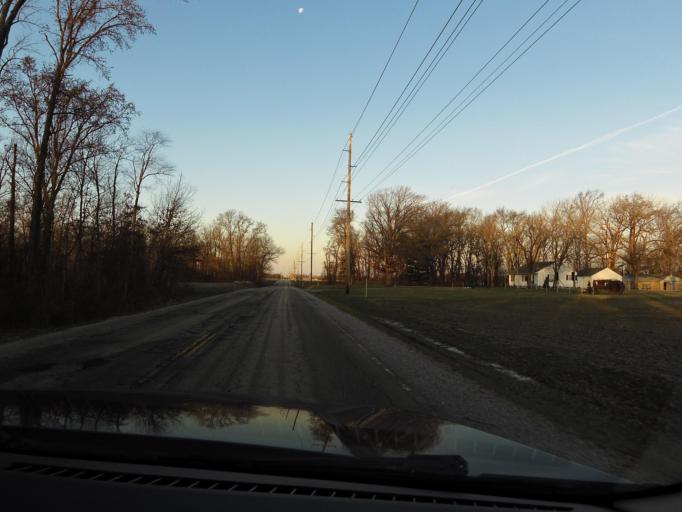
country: US
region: Illinois
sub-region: Marion County
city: Odin
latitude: 38.7650
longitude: -89.0620
